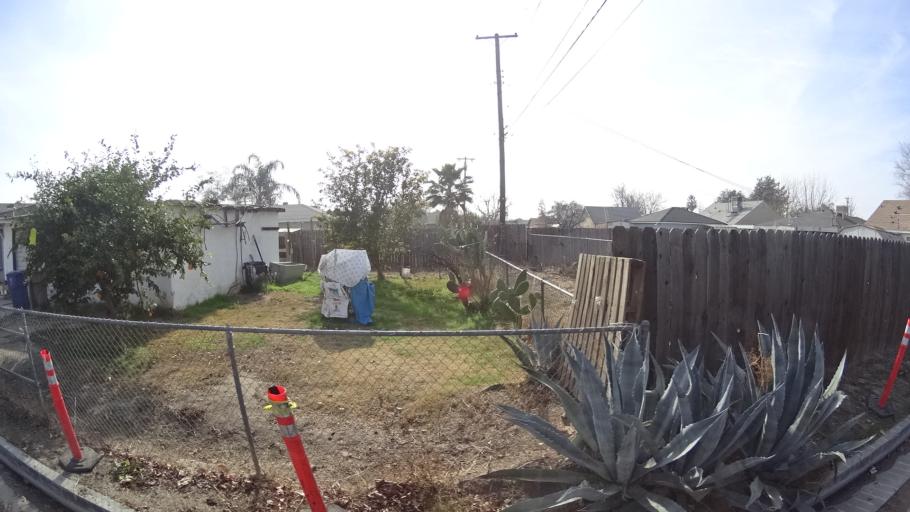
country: US
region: California
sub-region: Kern County
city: Bakersfield
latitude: 35.3430
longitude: -119.0170
